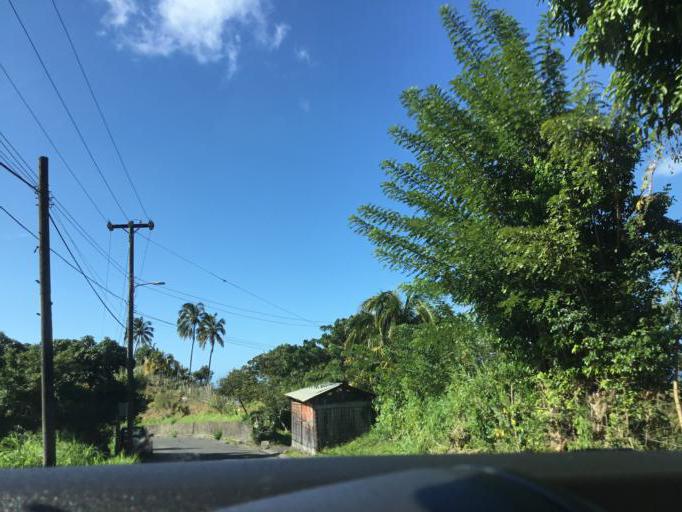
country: VC
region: Saint David
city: Chateaubelair
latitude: 13.2741
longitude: -61.2442
